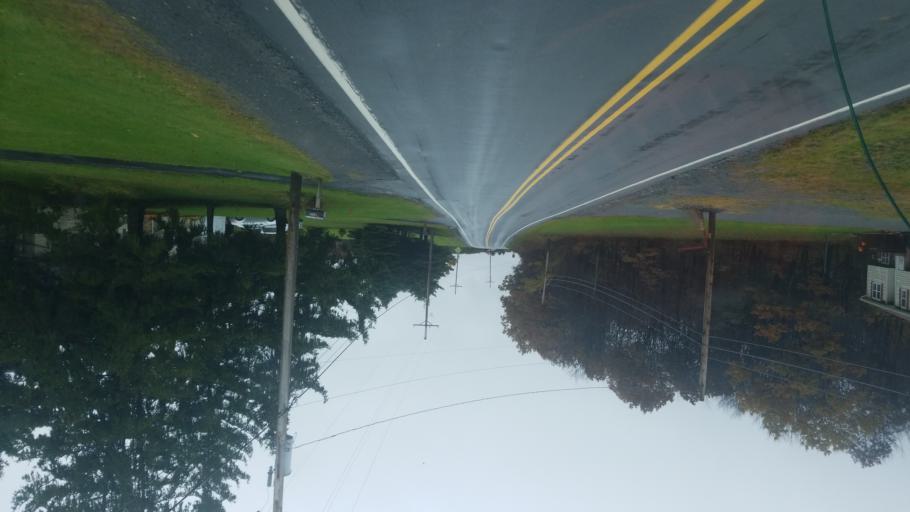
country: US
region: Pennsylvania
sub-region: Centre County
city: Milesburg
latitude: 41.0283
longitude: -77.9699
